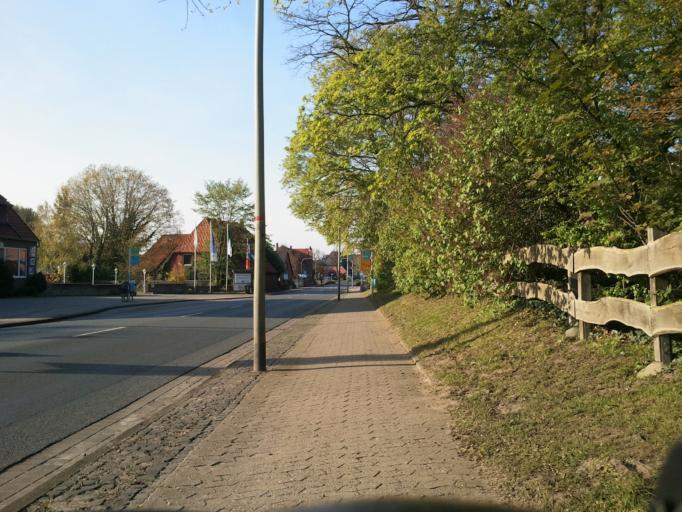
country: DE
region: Lower Saxony
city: Drakenburg
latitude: 52.6744
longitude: 9.2261
